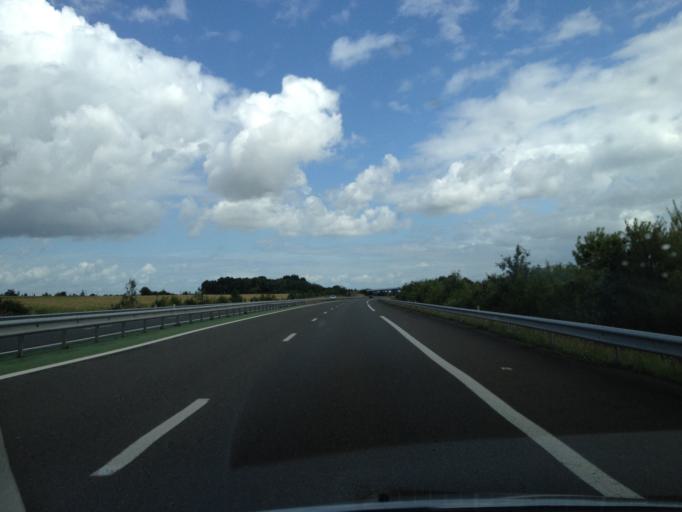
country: FR
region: Pays de la Loire
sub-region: Departement de Maine-et-Loire
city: Chemille-Melay
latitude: 47.1963
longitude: -0.7738
